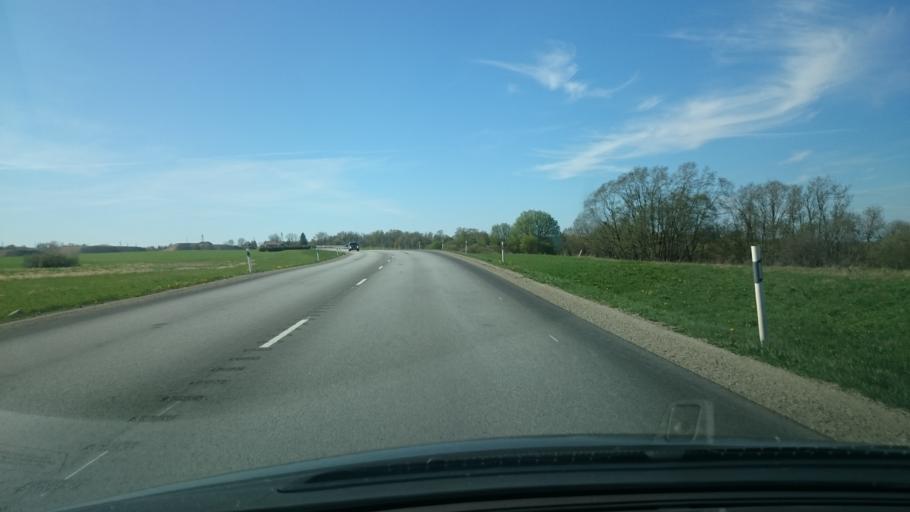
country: EE
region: Ida-Virumaa
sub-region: Kivioli linn
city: Kivioli
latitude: 59.4249
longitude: 26.9622
